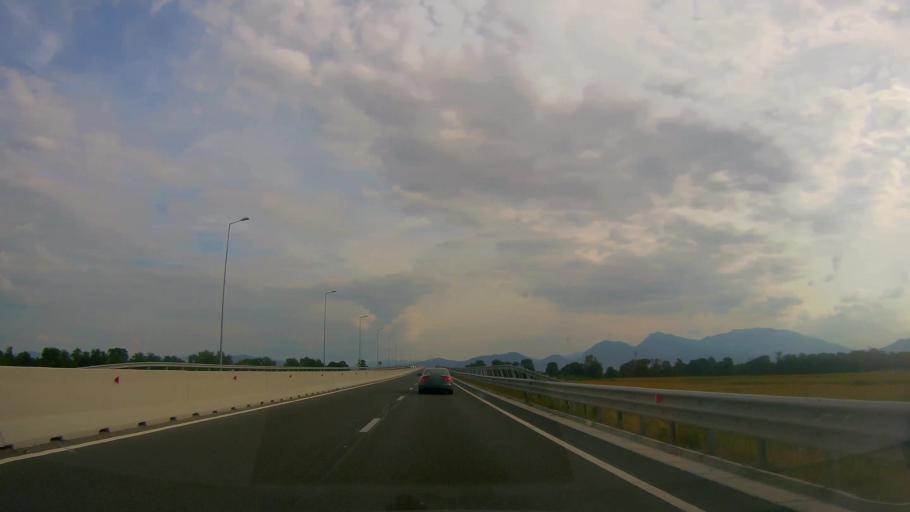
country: RO
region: Brasov
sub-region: Comuna Harman
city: Harman
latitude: 45.6802
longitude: 25.6700
